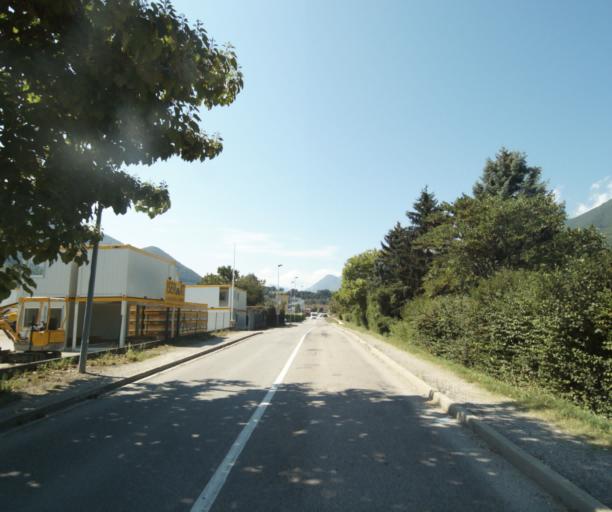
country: FR
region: Rhone-Alpes
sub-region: Departement de l'Isere
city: Vif
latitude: 45.0558
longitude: 5.6803
